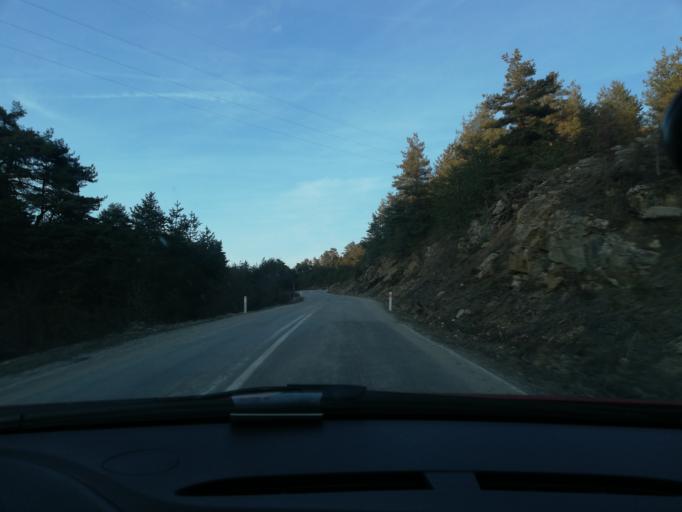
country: TR
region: Kastamonu
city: Agli
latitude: 41.7090
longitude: 33.6525
